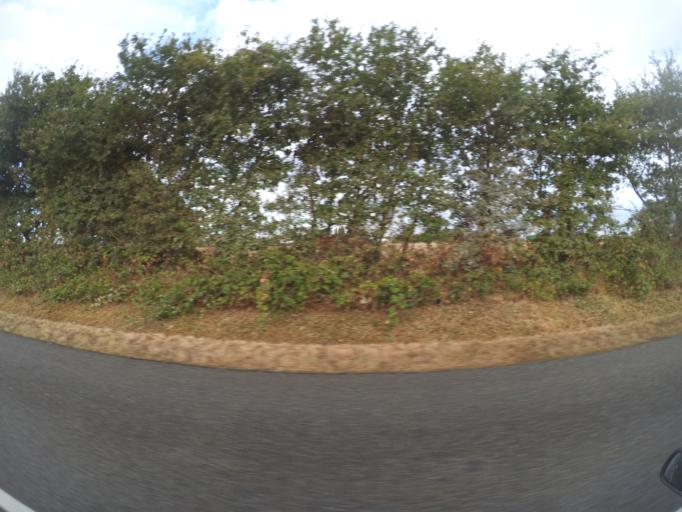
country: FR
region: Pays de la Loire
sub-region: Departement de la Loire-Atlantique
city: La Planche
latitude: 47.0168
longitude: -1.4234
